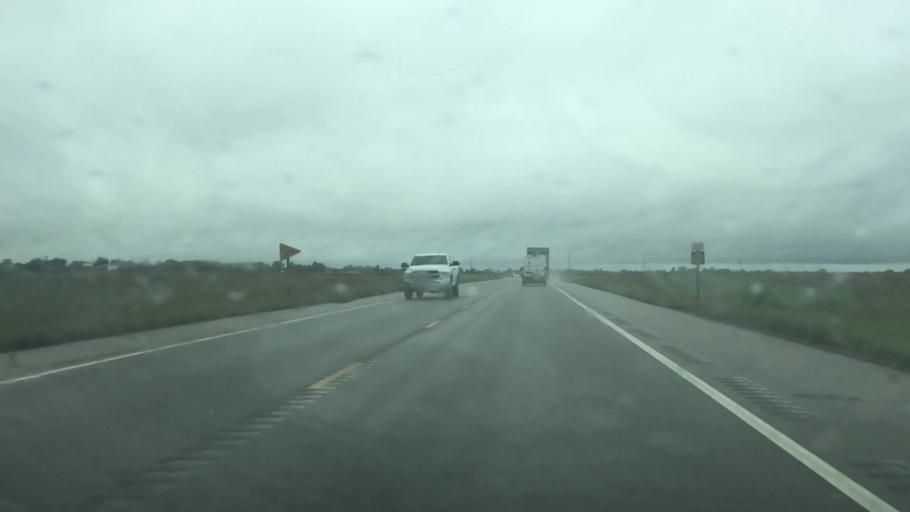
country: US
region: Kansas
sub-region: Allen County
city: Iola
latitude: 38.0844
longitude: -95.3681
